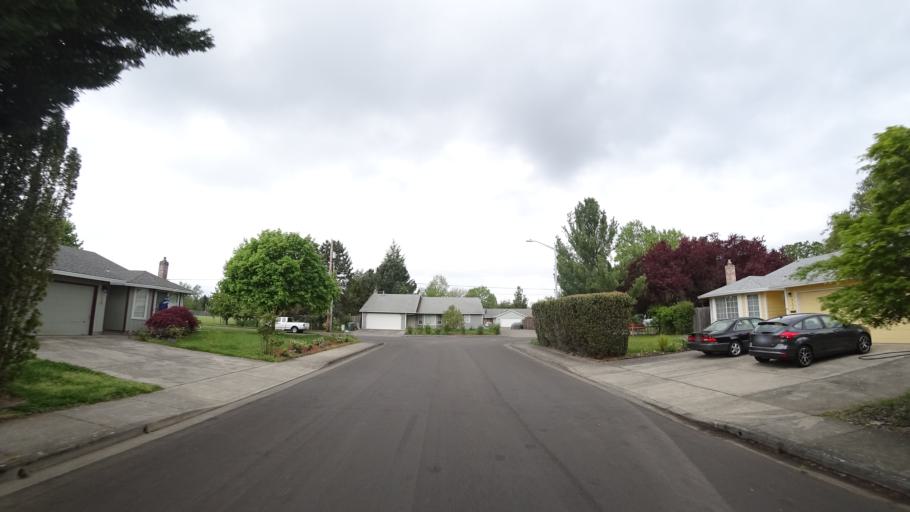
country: US
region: Oregon
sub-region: Washington County
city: Hillsboro
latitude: 45.5422
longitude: -122.9749
